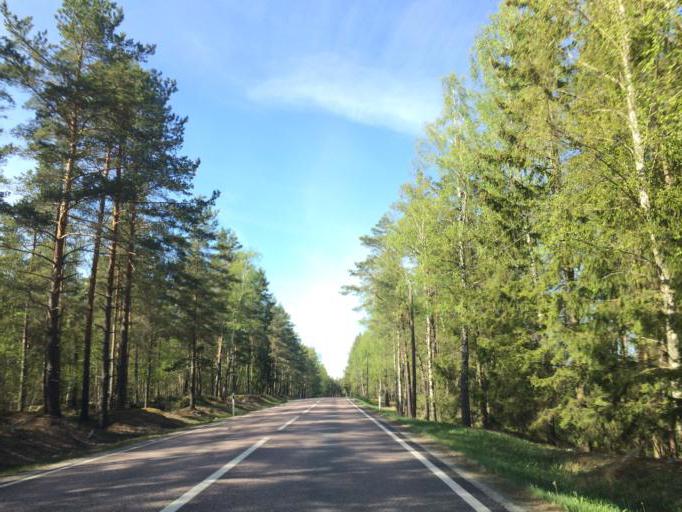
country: SE
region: Vaestmanland
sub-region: Kungsors Kommun
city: Kungsoer
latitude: 59.3328
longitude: 16.1118
